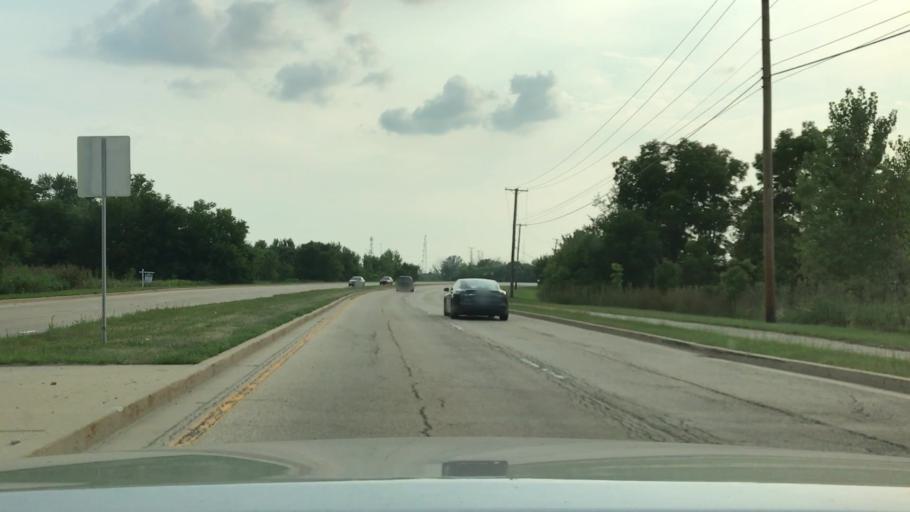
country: US
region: Illinois
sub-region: DuPage County
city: Warrenville
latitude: 41.8094
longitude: -88.2181
